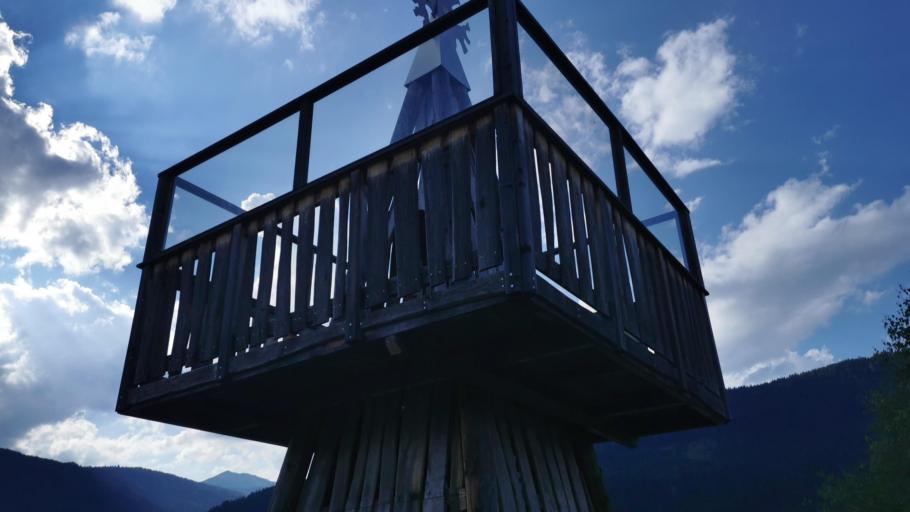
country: AT
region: Salzburg
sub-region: Politischer Bezirk Tamsweg
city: Sankt Margarethen im Lungau
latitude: 47.0971
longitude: 13.7198
